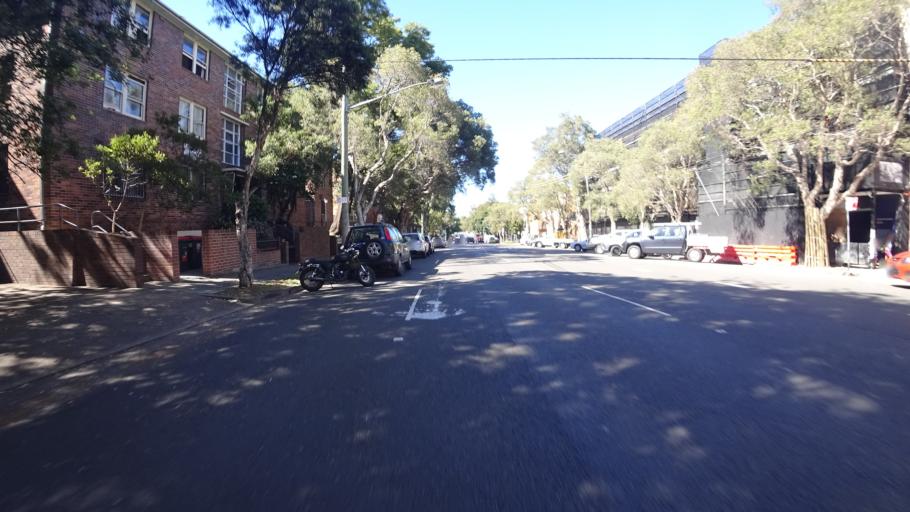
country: AU
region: New South Wales
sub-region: City of Sydney
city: Redfern
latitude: -33.8919
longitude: 151.2076
